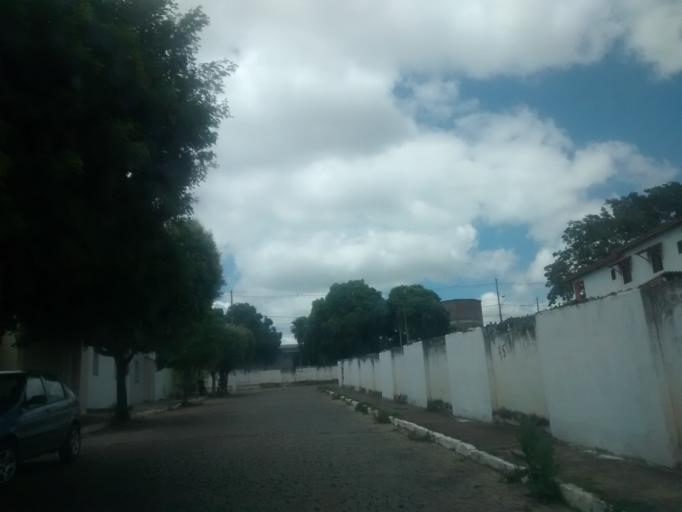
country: BR
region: Bahia
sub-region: Brumado
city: Brumado
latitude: -14.2027
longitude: -41.6739
